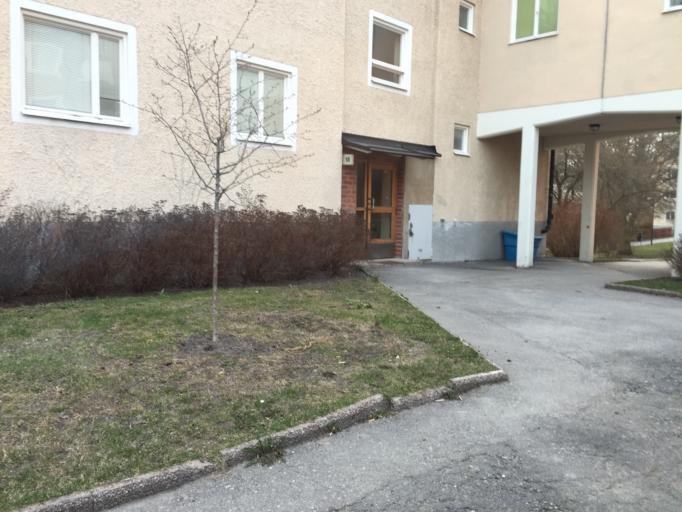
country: SE
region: Stockholm
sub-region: Stockholms Kommun
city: Bromma
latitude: 59.3577
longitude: 17.8866
